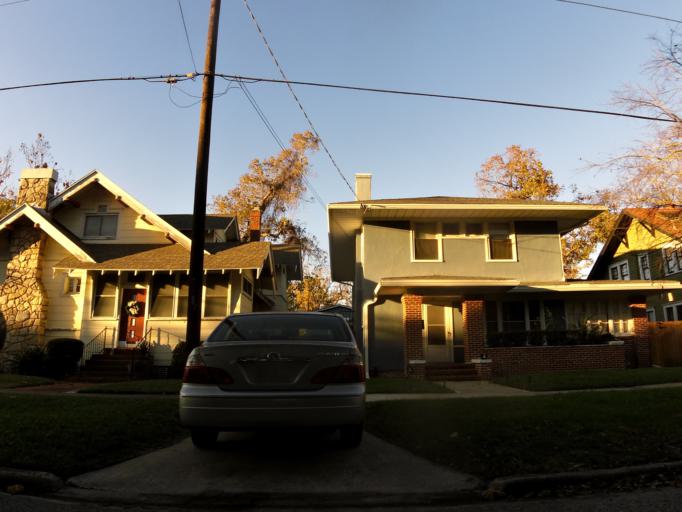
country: US
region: Florida
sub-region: Duval County
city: Jacksonville
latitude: 30.3179
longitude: -81.6841
